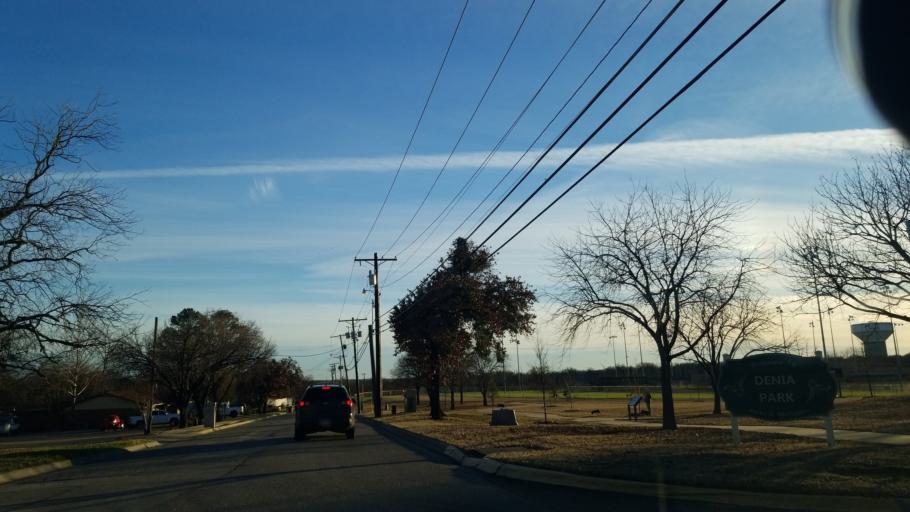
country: US
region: Texas
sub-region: Denton County
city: Denton
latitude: 33.1907
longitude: -97.1418
